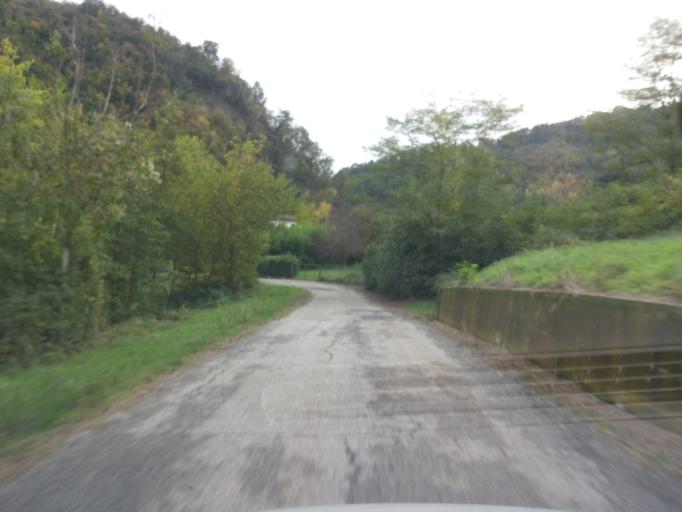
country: IT
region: Piedmont
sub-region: Provincia di Alessandria
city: Serralunga di Crea
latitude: 45.0990
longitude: 8.2874
